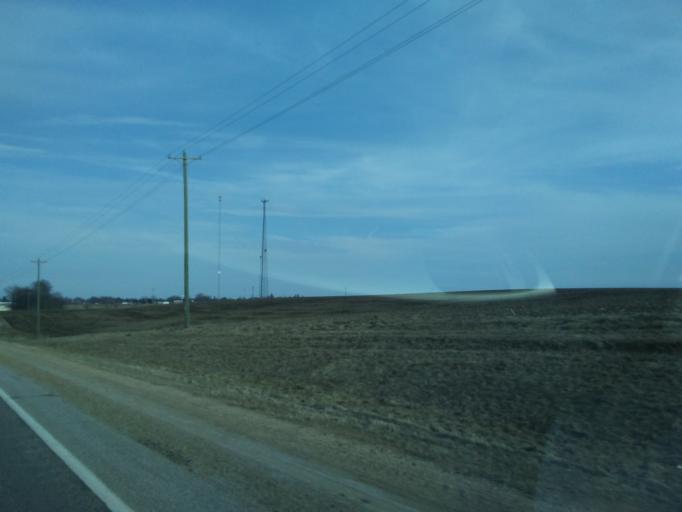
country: US
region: Wisconsin
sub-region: Grant County
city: Fennimore
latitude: 42.9883
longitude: -90.6805
